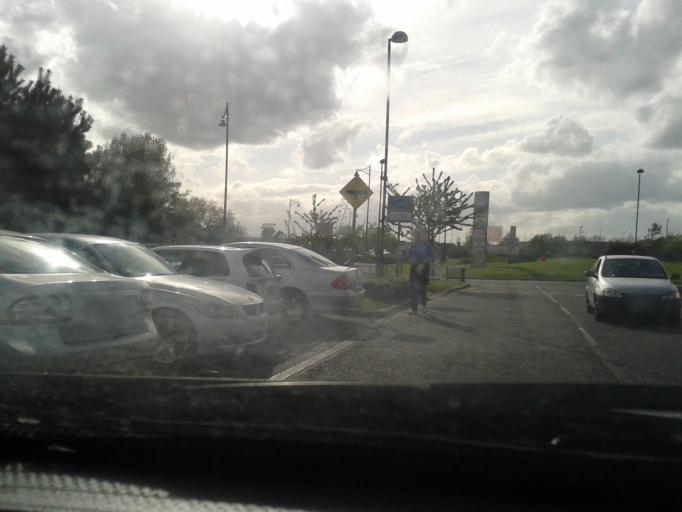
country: IE
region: Leinster
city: Ballymun
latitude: 53.4036
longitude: -6.2604
